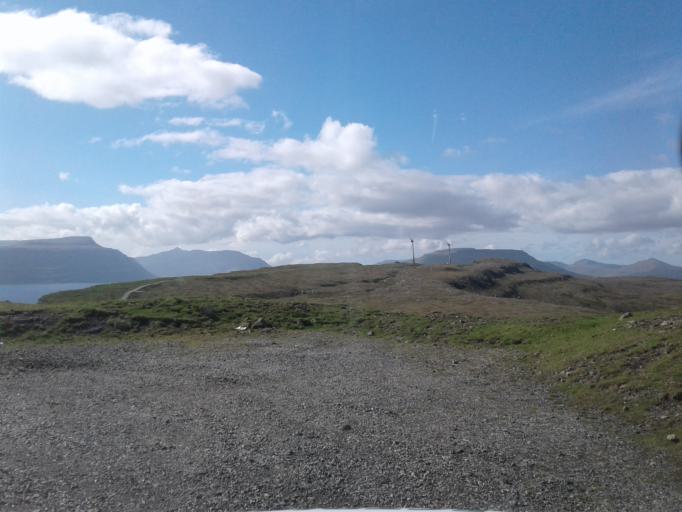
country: FO
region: Streymoy
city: Hoyvik
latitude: 62.0594
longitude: -6.6935
